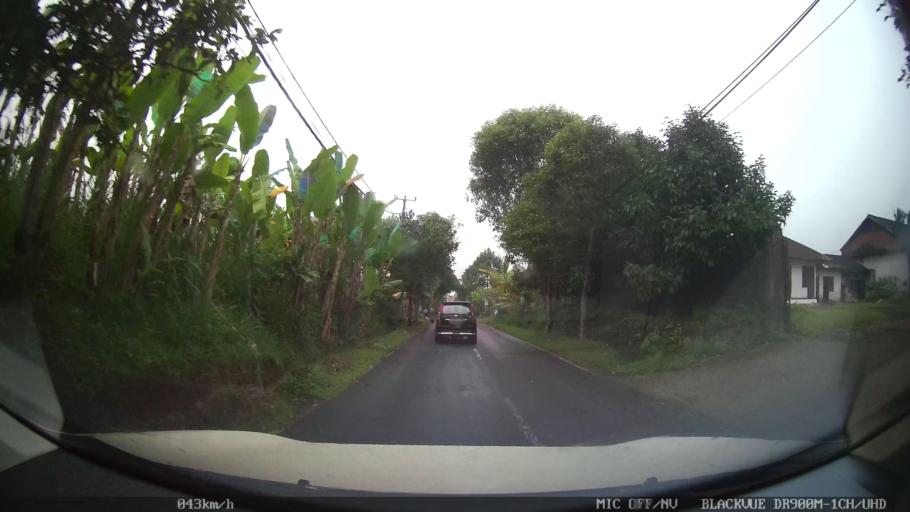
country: ID
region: Bali
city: Banjar Taro Kelod
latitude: -8.3753
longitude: 115.2677
